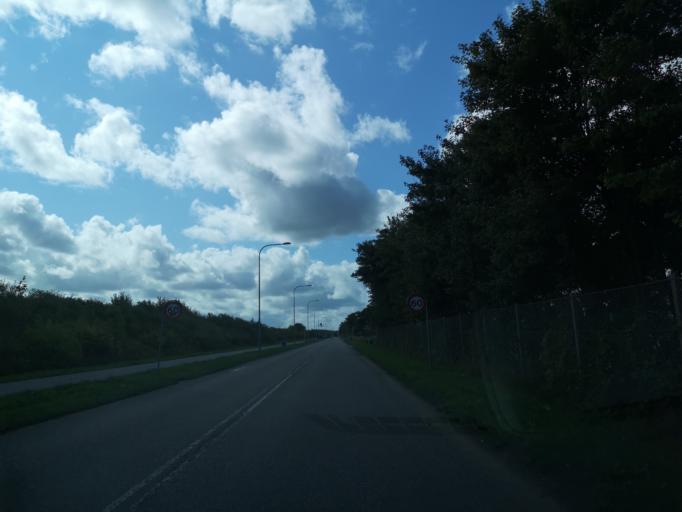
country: DK
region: Central Jutland
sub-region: Holstebro Kommune
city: Holstebro
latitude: 56.3902
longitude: 8.5806
